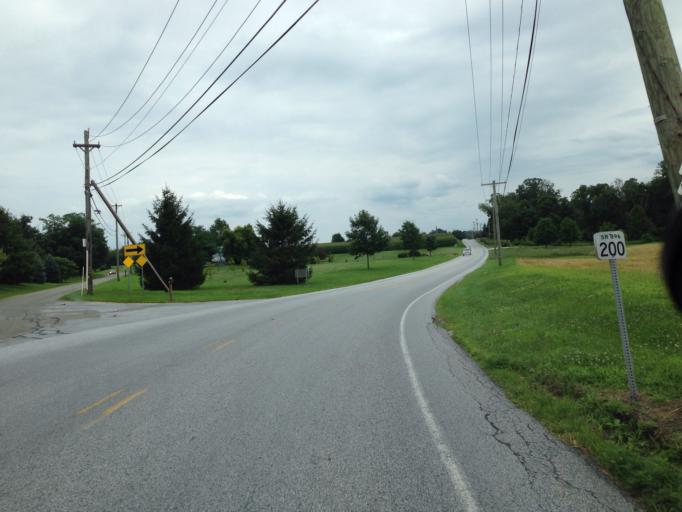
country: US
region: Pennsylvania
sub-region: Chester County
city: Oxford
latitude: 39.8379
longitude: -75.9324
